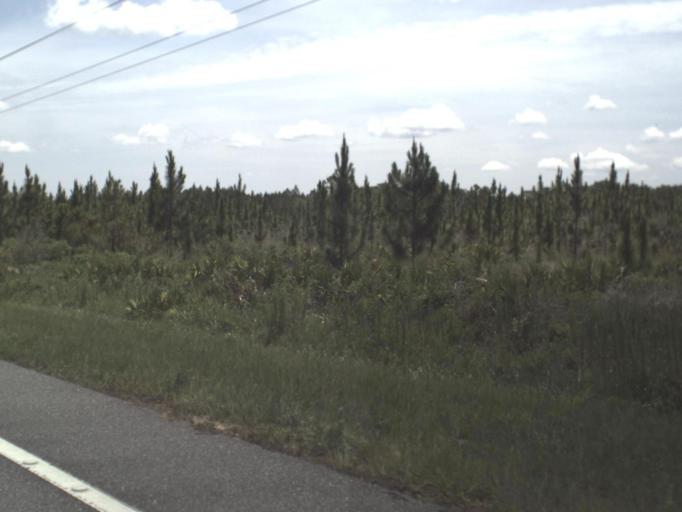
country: US
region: Florida
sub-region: Taylor County
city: Steinhatchee
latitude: 29.7665
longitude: -83.3402
